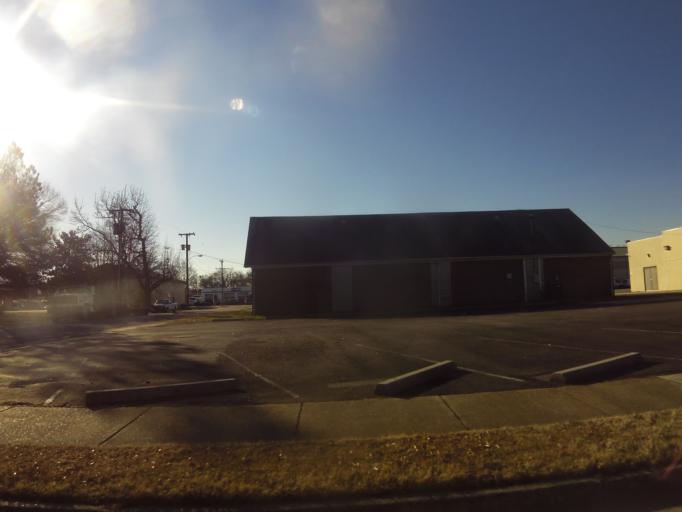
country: US
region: Virginia
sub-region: City of Hopewell
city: Hopewell
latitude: 37.3024
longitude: -77.2939
